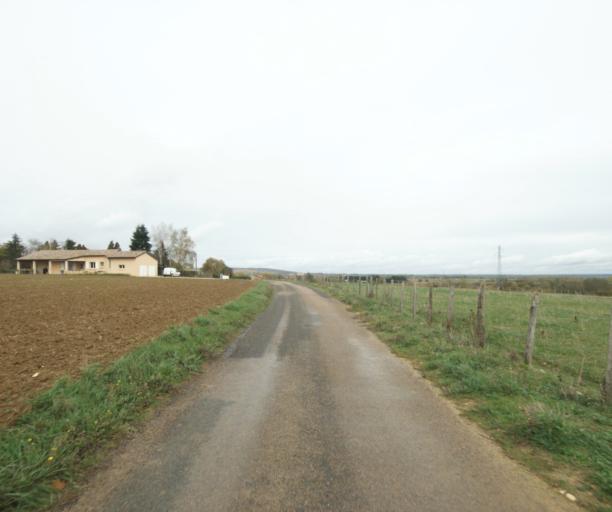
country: FR
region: Rhone-Alpes
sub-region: Departement de l'Ain
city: Pont-de-Vaux
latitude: 46.4705
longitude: 4.8738
